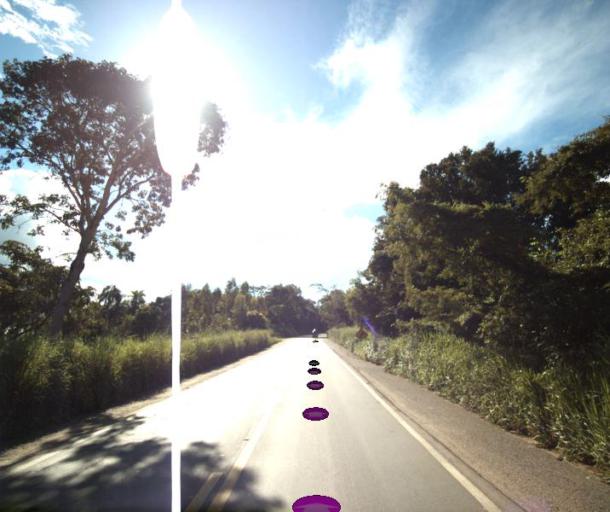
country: BR
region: Goias
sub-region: Uruana
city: Uruana
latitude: -15.4943
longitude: -49.4871
